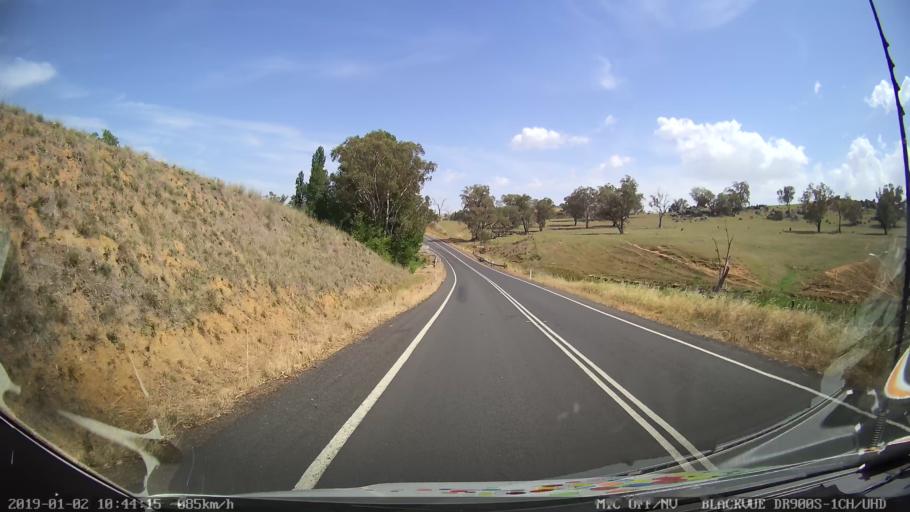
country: AU
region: New South Wales
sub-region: Cootamundra
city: Cootamundra
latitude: -34.7628
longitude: 148.2977
